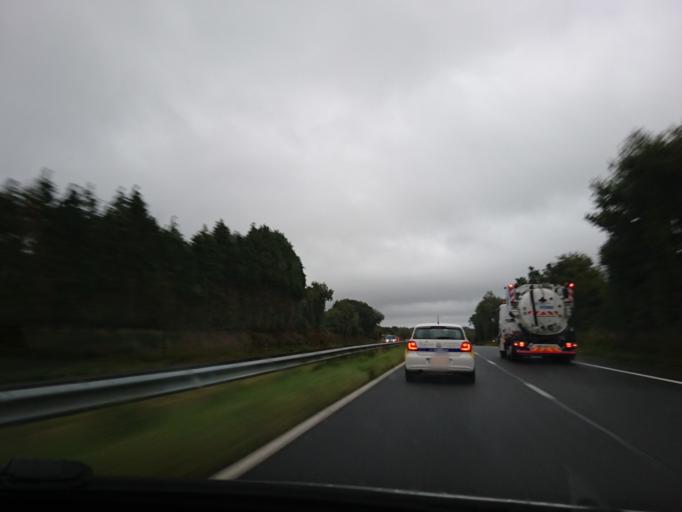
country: FR
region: Brittany
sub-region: Departement du Finistere
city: Loperhet
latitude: 48.3834
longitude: -4.3228
